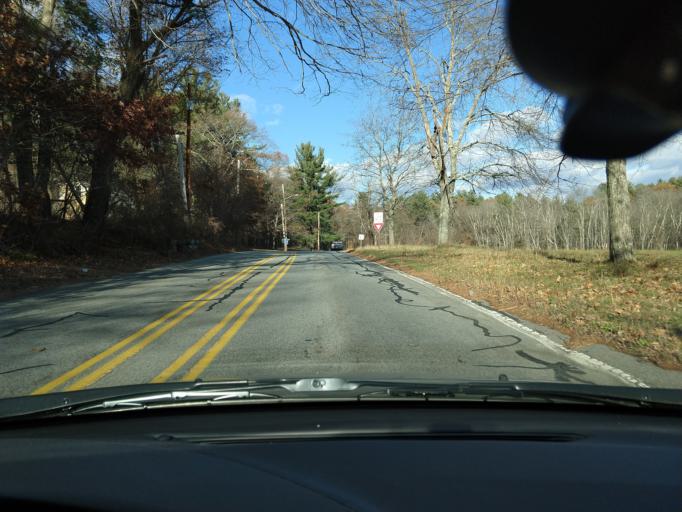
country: US
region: Massachusetts
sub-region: Middlesex County
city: West Concord
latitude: 42.4299
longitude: -71.3757
